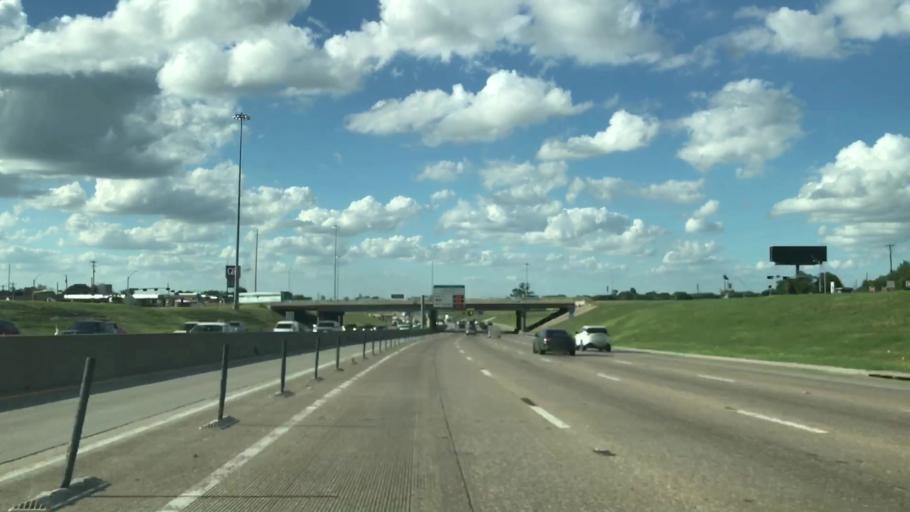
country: US
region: Texas
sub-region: Dallas County
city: Richardson
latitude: 32.8929
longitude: -96.7105
